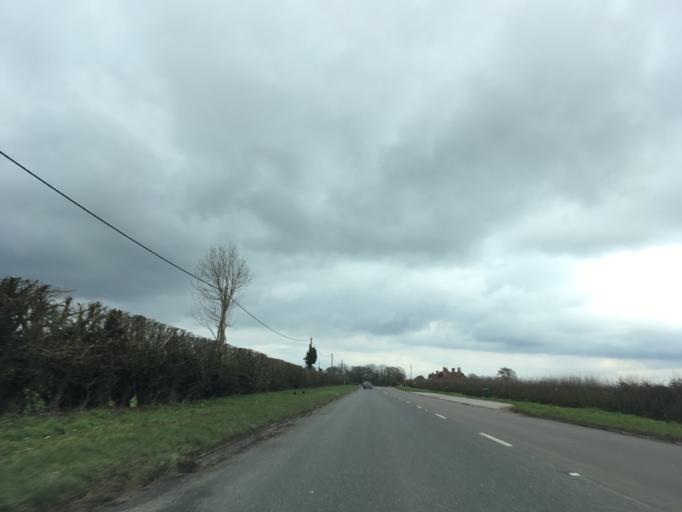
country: GB
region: England
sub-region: West Berkshire
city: Kintbury
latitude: 51.4134
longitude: -1.4263
